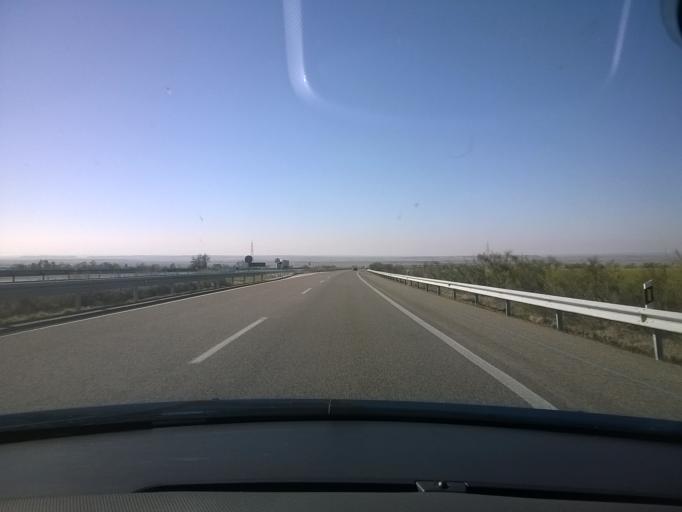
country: ES
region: Aragon
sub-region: Provincia de Zaragoza
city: Mequinensa / Mequinenza
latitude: 41.4677
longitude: 0.2420
